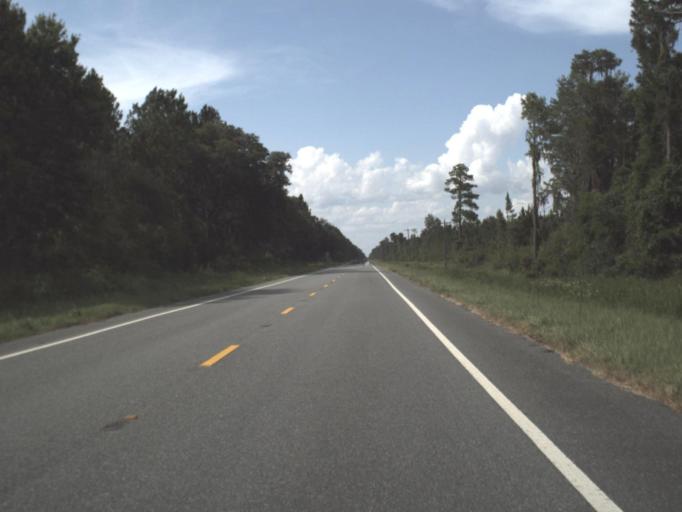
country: US
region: Florida
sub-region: Taylor County
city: Perry
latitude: 30.2206
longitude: -83.6145
